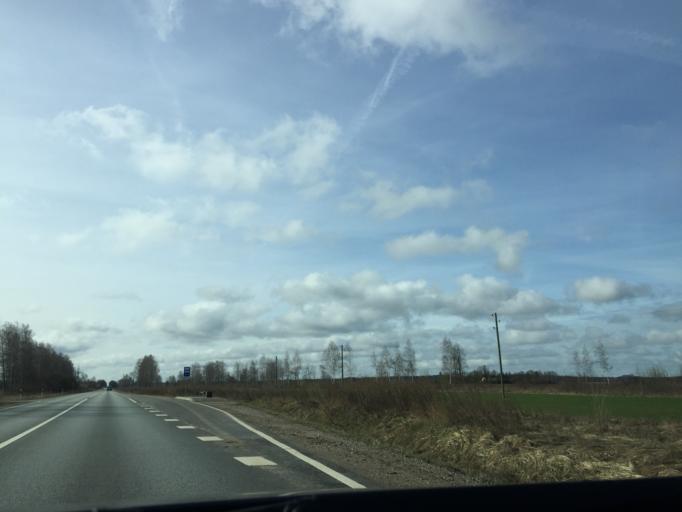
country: LT
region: Siauliu apskritis
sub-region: Joniskis
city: Joniskis
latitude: 56.4387
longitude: 23.6879
